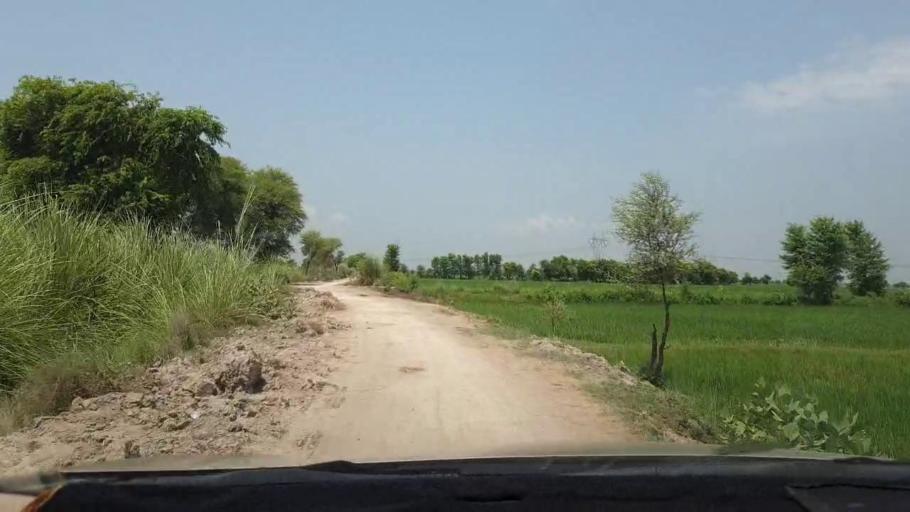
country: PK
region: Sindh
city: Naudero
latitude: 27.6643
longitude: 68.3125
